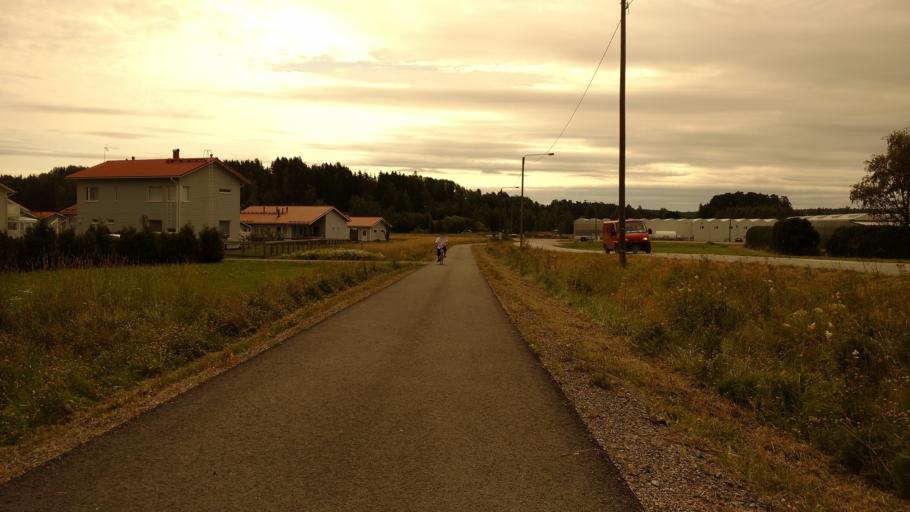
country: FI
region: Varsinais-Suomi
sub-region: Turku
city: Piikkioe
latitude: 60.4271
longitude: 22.4838
